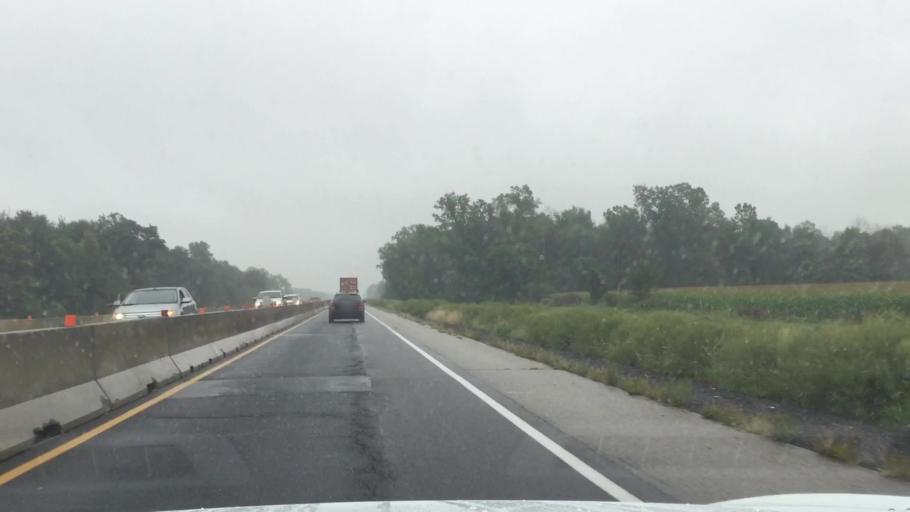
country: CA
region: Ontario
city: Delaware
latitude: 42.7961
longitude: -81.3453
